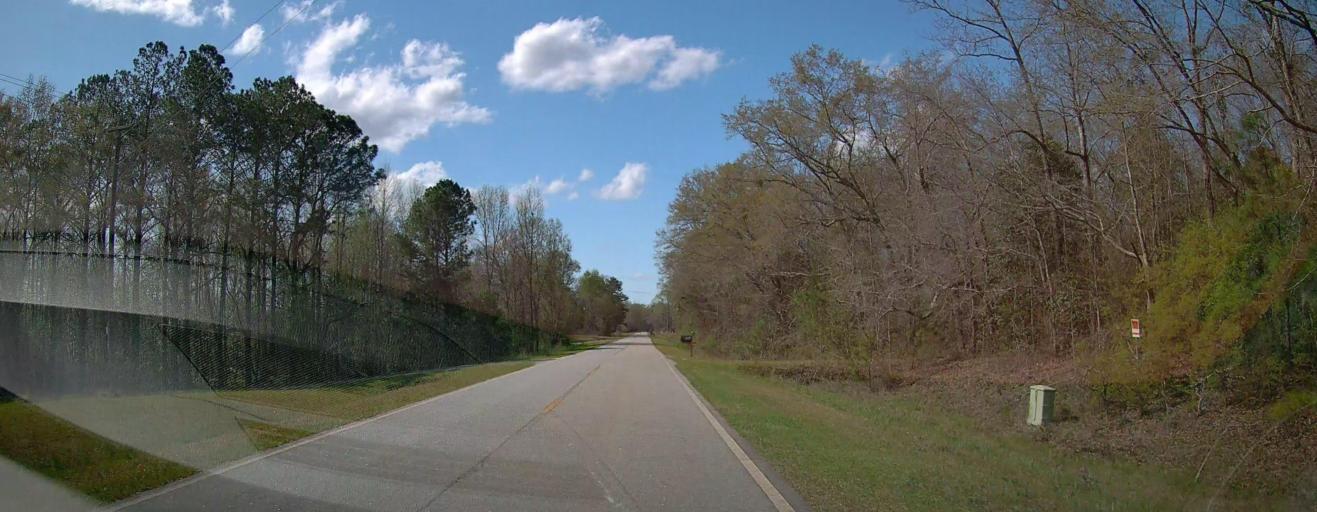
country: US
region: Georgia
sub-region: Wilkinson County
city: Gordon
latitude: 32.8426
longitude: -83.4428
